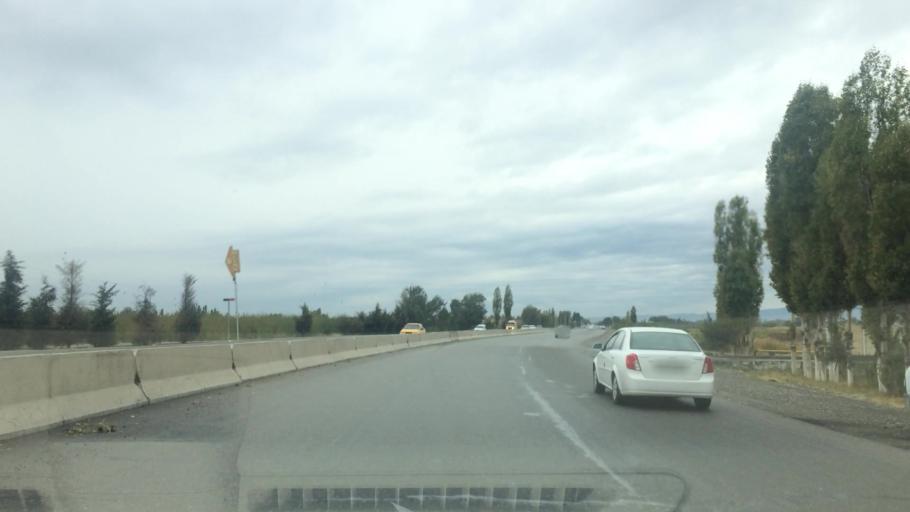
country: UZ
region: Jizzax
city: Jizzax
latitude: 40.0218
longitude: 67.6145
